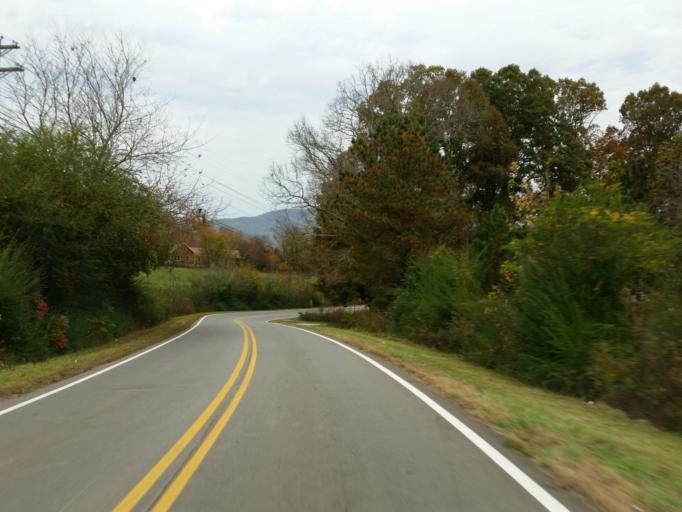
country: US
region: Georgia
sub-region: Gilmer County
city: Ellijay
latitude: 34.6485
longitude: -84.3879
